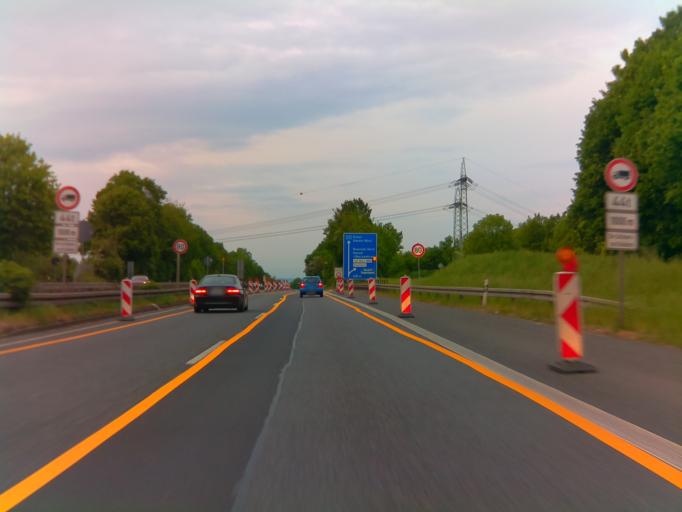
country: DE
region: Hesse
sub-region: Regierungsbezirk Kassel
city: Baunatal
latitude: 51.2503
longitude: 9.4393
